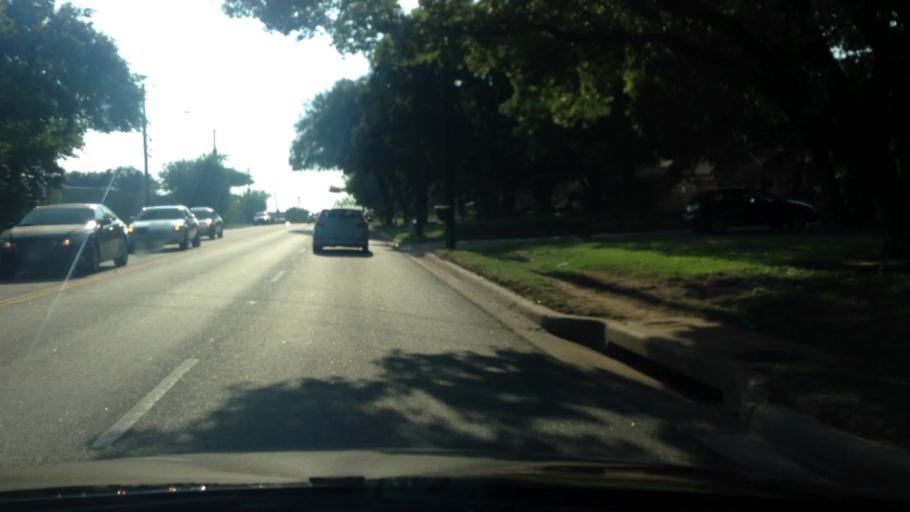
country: US
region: Texas
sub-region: Tarrant County
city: Edgecliff Village
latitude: 32.6351
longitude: -97.3416
